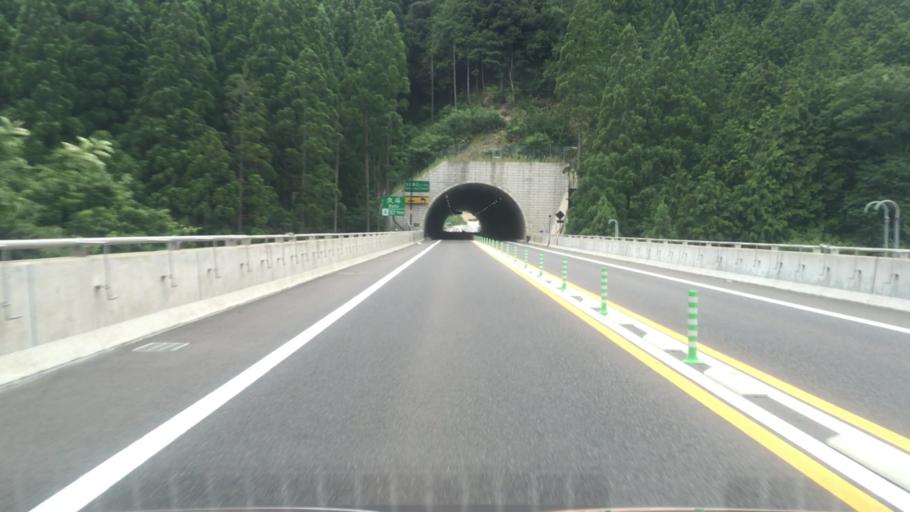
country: JP
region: Tottori
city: Tottori
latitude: 35.6241
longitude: 134.5148
